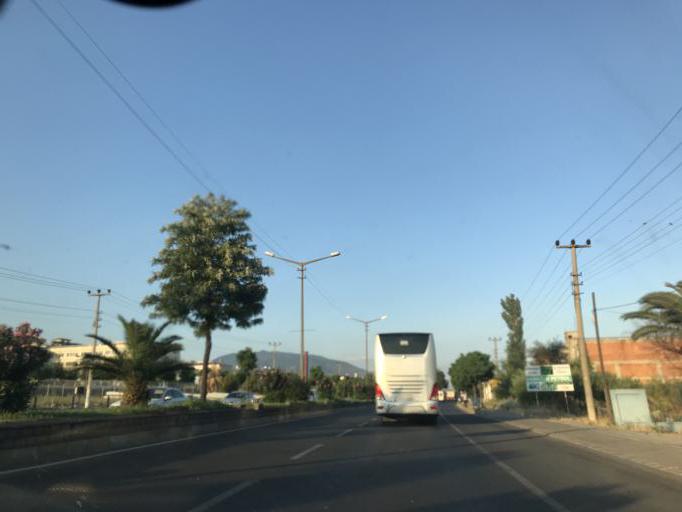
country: TR
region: Aydin
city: Nazilli
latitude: 37.9137
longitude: 28.3474
